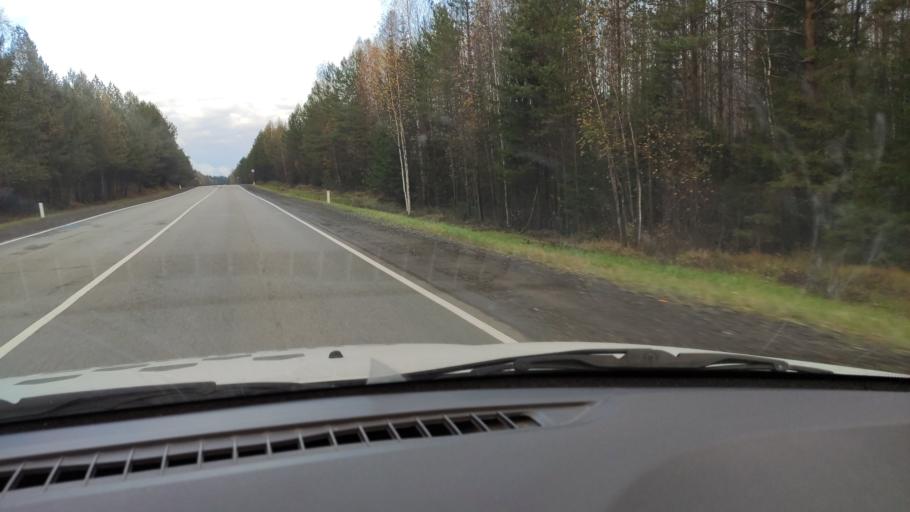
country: RU
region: Kirov
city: Belaya Kholunitsa
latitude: 58.8977
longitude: 50.9226
